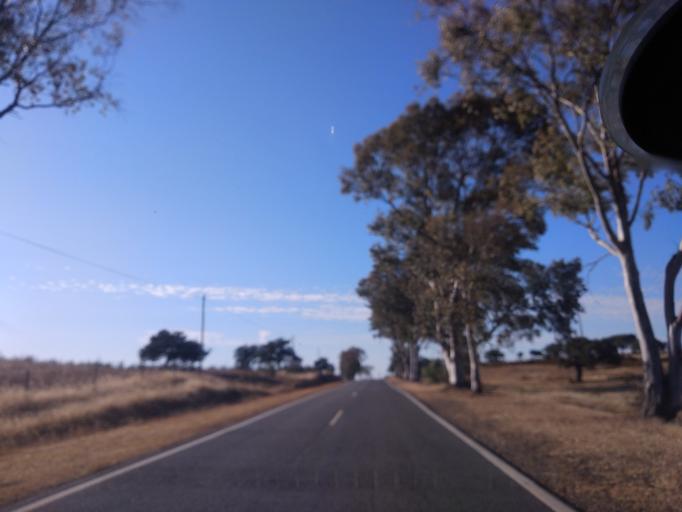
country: PT
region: Beja
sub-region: Almodovar
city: Almodovar
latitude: 37.4456
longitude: -7.9957
